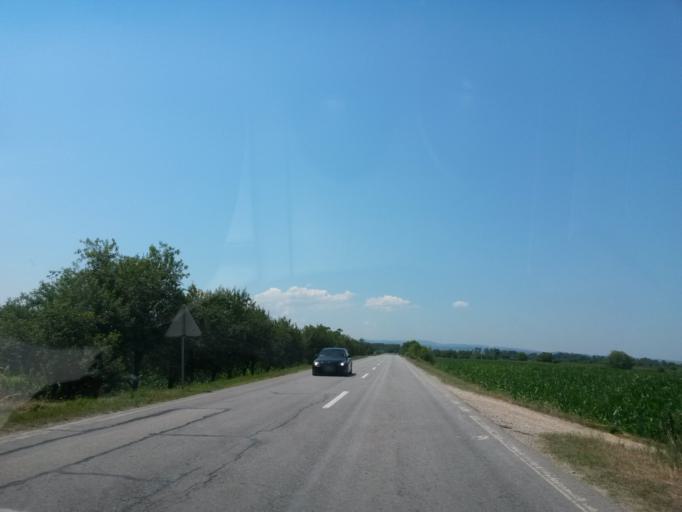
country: BA
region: Federation of Bosnia and Herzegovina
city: Odzak
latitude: 45.0044
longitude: 18.3910
